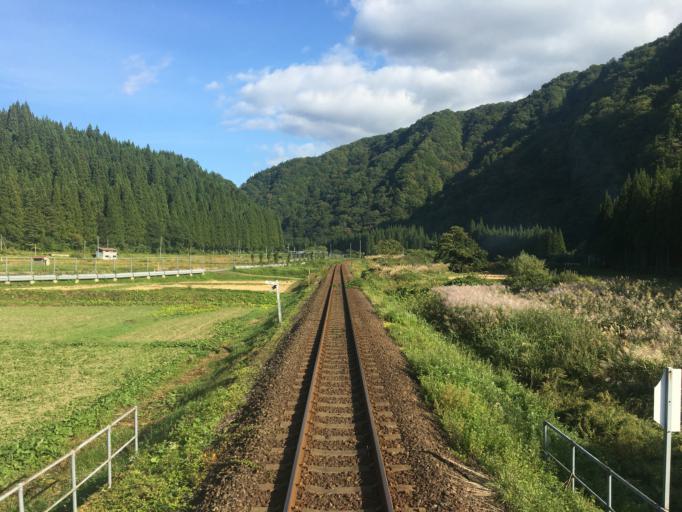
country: JP
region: Akita
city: Kakunodatemachi
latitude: 39.9188
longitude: 140.5182
